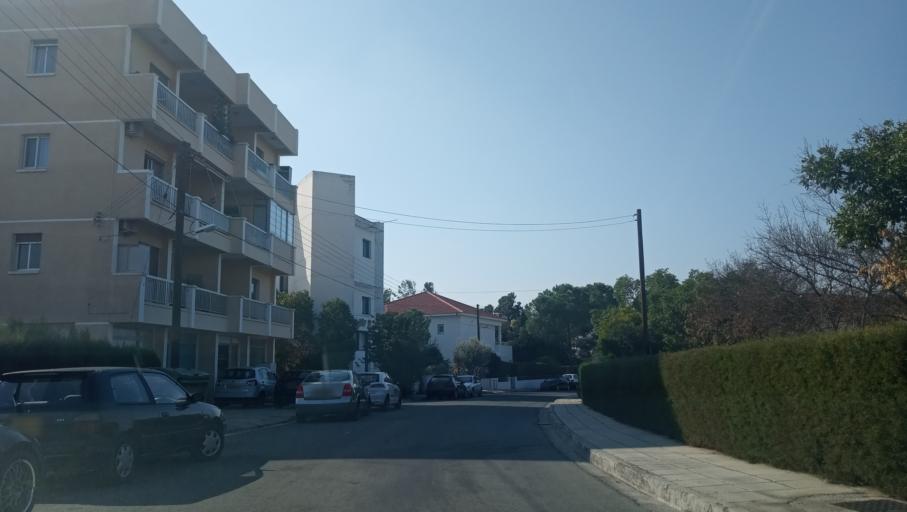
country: CY
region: Lefkosia
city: Nicosia
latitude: 35.1470
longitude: 33.3932
